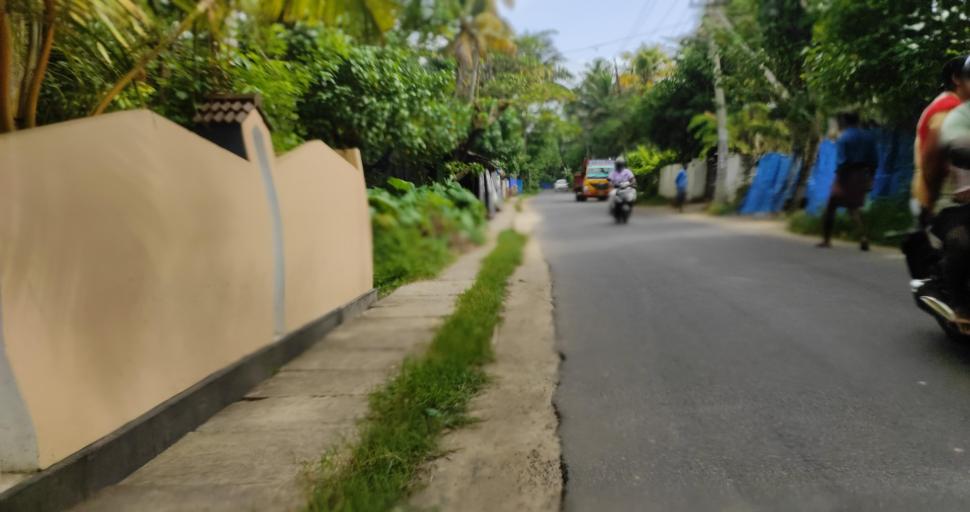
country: IN
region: Kerala
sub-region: Alappuzha
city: Vayalar
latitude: 9.7361
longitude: 76.2861
